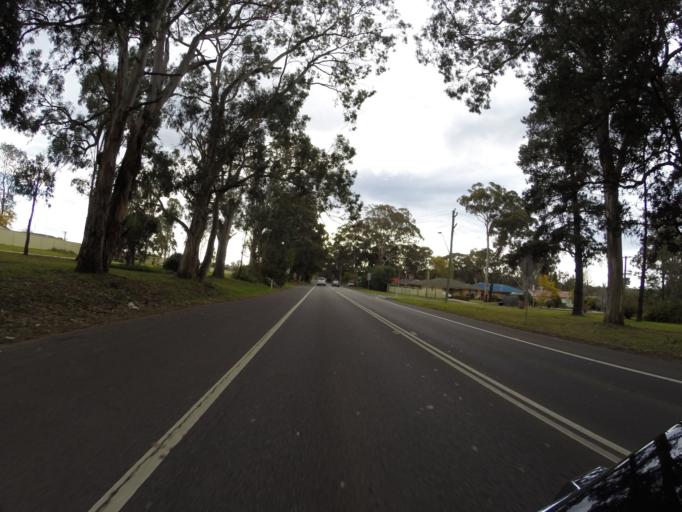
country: AU
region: New South Wales
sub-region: Wollondilly
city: Douglas Park
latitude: -34.1963
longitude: 150.7891
